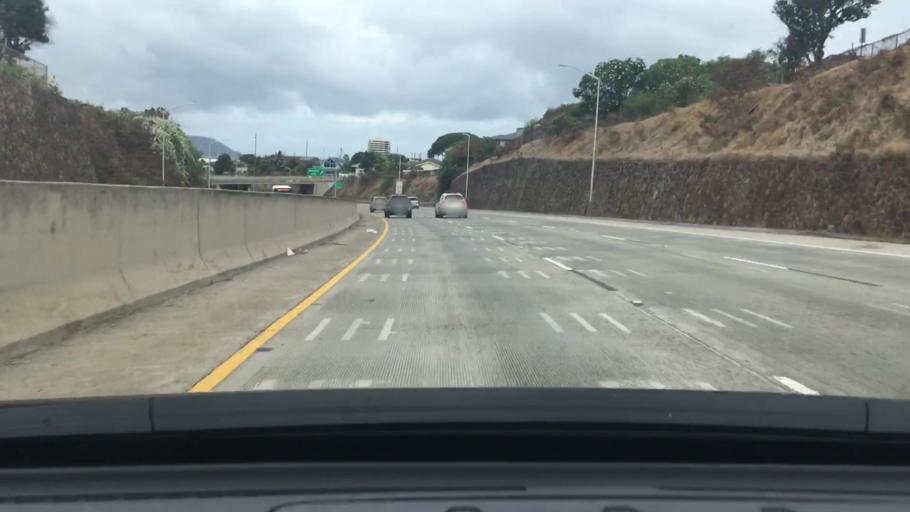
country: US
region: Hawaii
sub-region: Honolulu County
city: Honolulu
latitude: 21.2790
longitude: -157.7977
